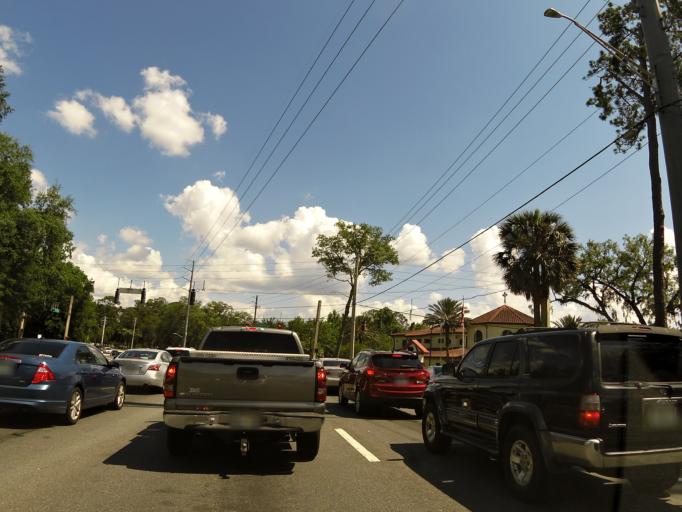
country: US
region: Florida
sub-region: Saint Johns County
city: Fruit Cove
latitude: 30.1609
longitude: -81.5998
